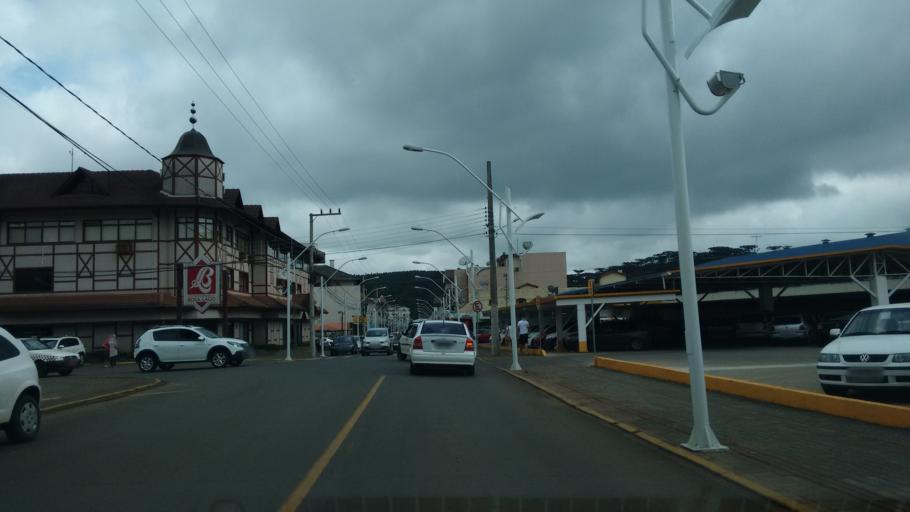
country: BR
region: Santa Catarina
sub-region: Videira
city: Videira
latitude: -27.0254
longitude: -50.9252
